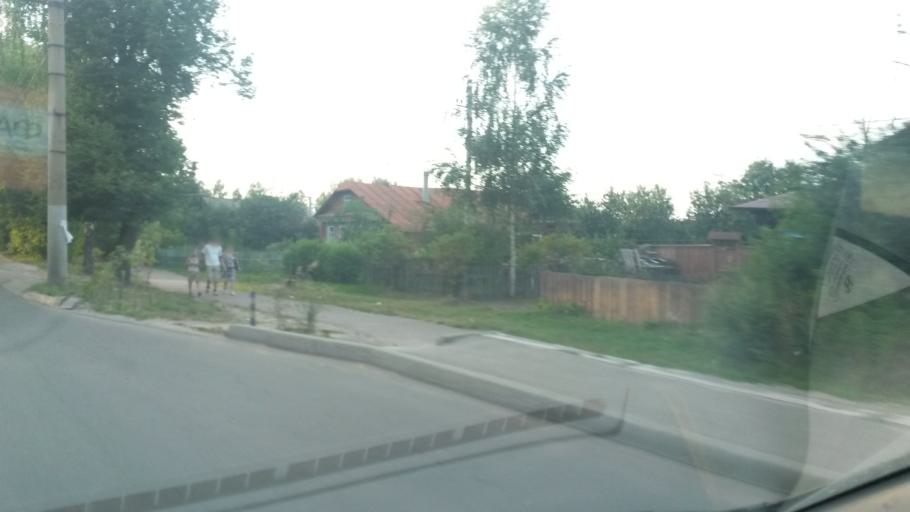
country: RU
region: Ivanovo
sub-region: Gorod Ivanovo
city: Ivanovo
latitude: 57.0123
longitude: 40.9370
